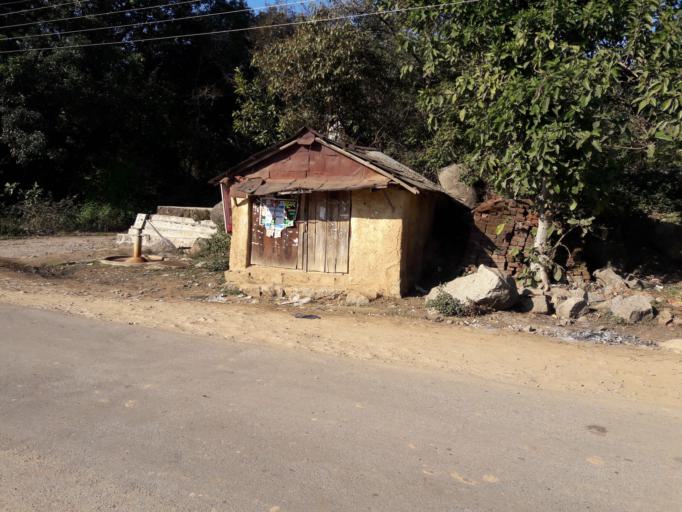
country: IN
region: Himachal Pradesh
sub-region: Kangra
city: Yol
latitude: 32.2014
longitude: 76.2161
